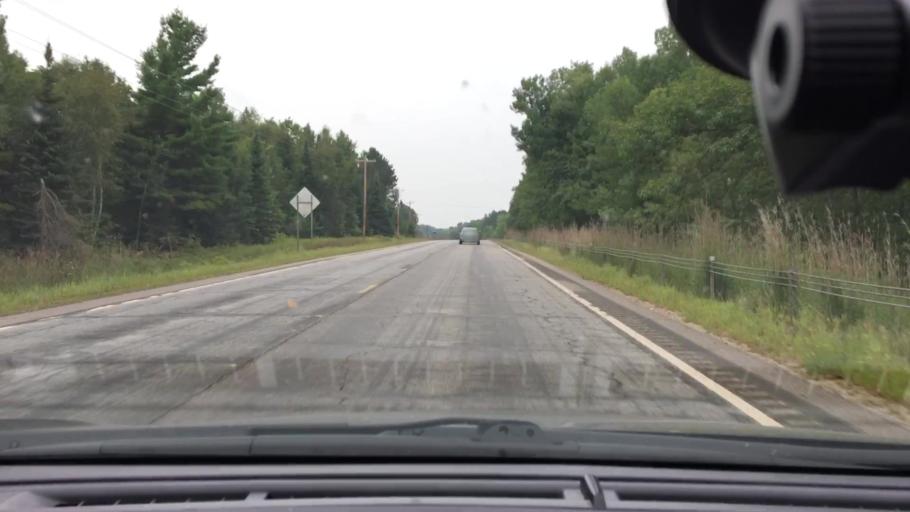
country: US
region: Minnesota
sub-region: Crow Wing County
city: Cross Lake
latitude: 46.8129
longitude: -93.9465
